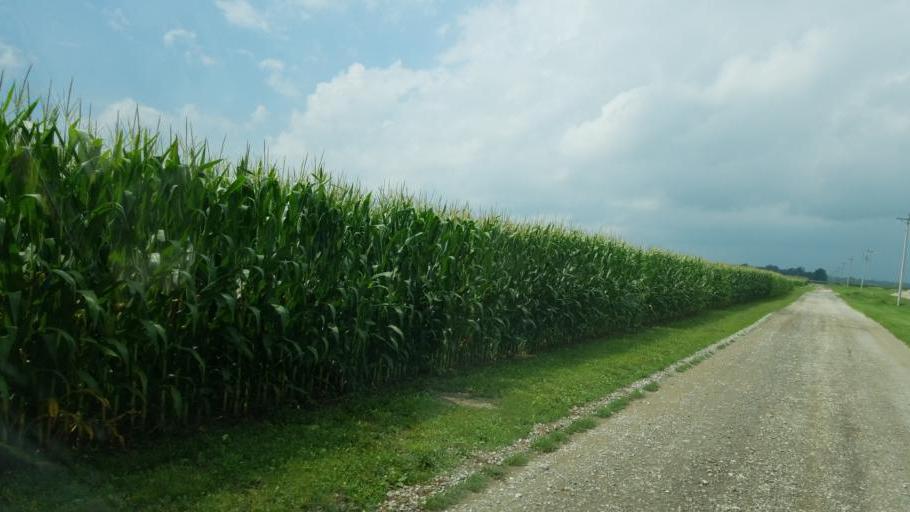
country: US
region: Ohio
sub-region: Union County
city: Richwood
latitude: 40.5309
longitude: -83.3266
